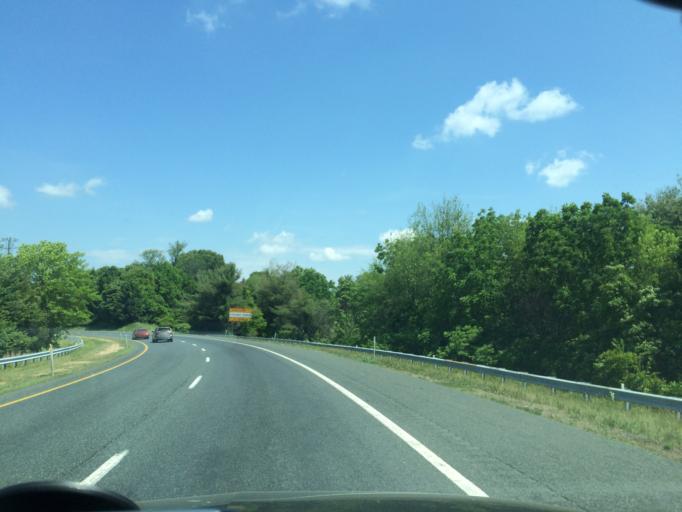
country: US
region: Maryland
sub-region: Baltimore County
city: Reisterstown
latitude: 39.4698
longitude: -76.8364
